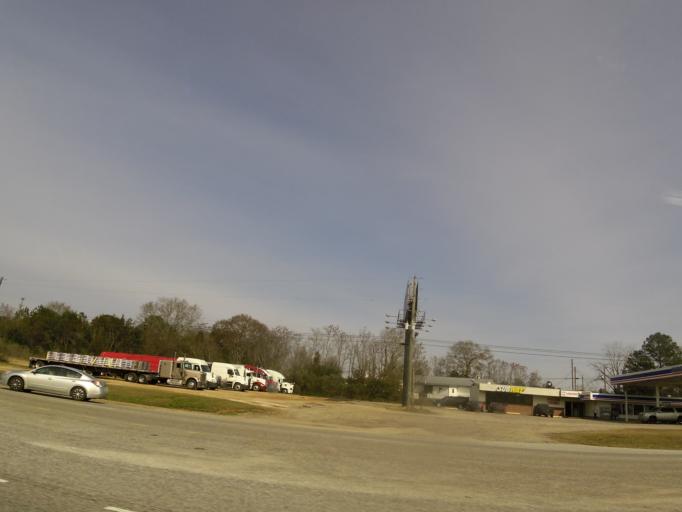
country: US
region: Alabama
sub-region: Dale County
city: Midland City
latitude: 31.2945
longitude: -85.4780
